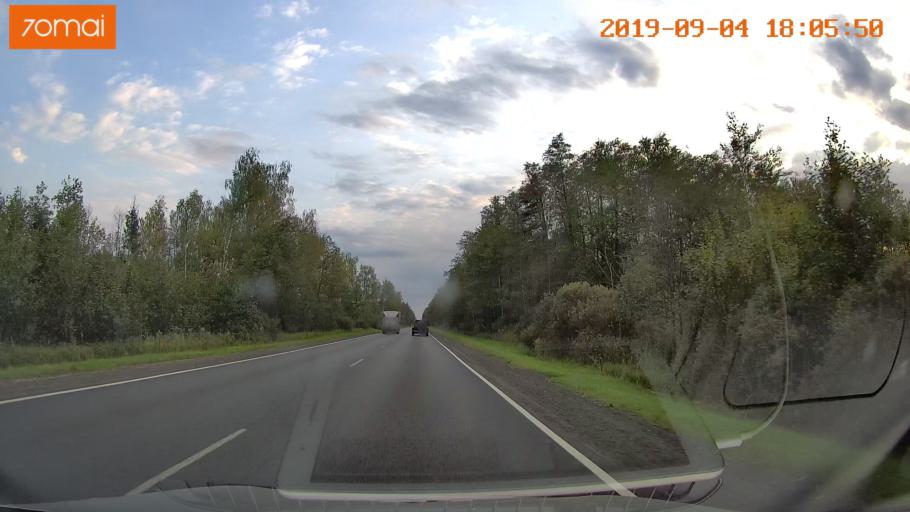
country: RU
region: Moskovskaya
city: Il'inskiy Pogost
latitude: 55.4372
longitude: 38.8218
